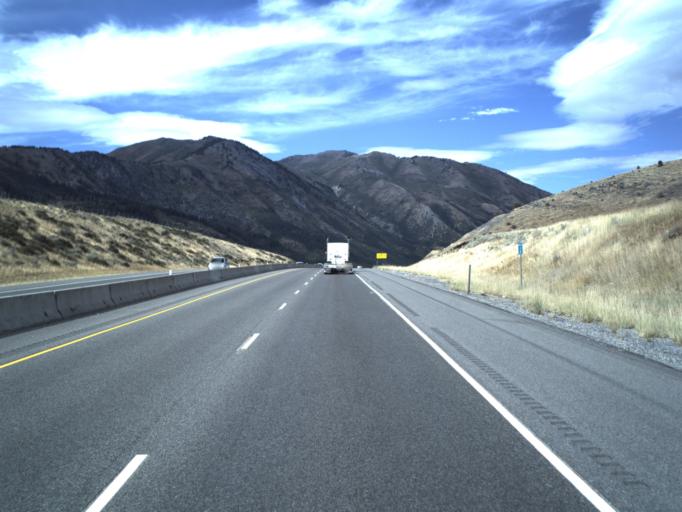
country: US
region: Utah
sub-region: Cache County
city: Wellsville
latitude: 41.5745
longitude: -111.9707
